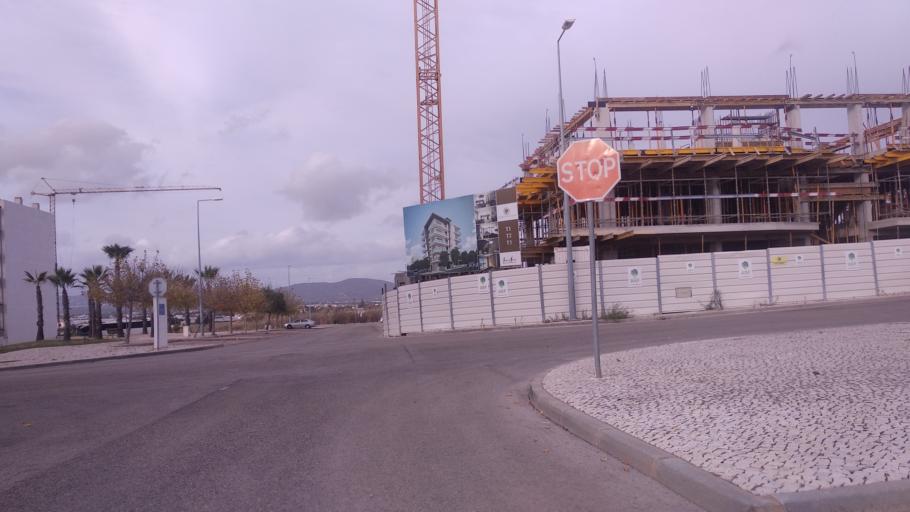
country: PT
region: Faro
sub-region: Faro
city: Faro
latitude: 37.0324
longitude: -7.9377
